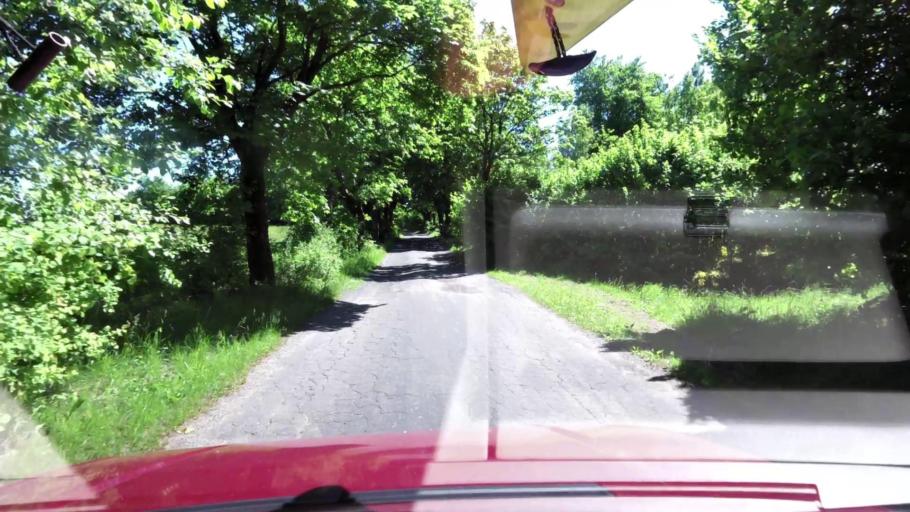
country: PL
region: West Pomeranian Voivodeship
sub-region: Powiat koszalinski
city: Polanow
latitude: 54.0405
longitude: 16.7576
